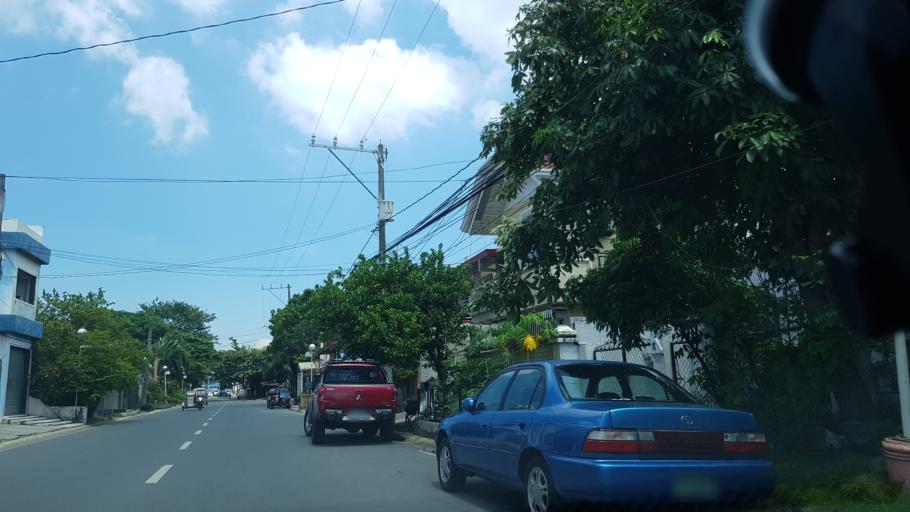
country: PH
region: Calabarzon
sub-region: Province of Rizal
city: Las Pinas
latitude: 14.4377
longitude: 120.9846
